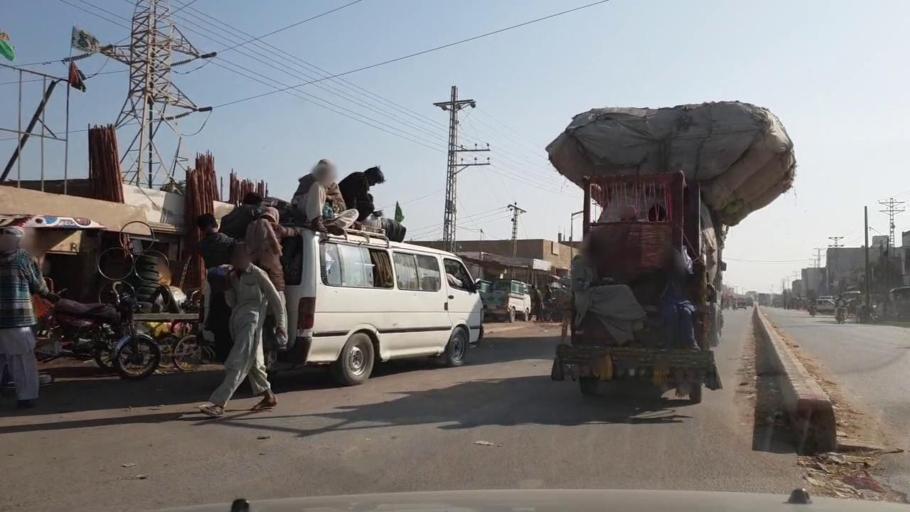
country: PK
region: Sindh
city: Tando Muhammad Khan
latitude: 25.1309
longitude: 68.5446
